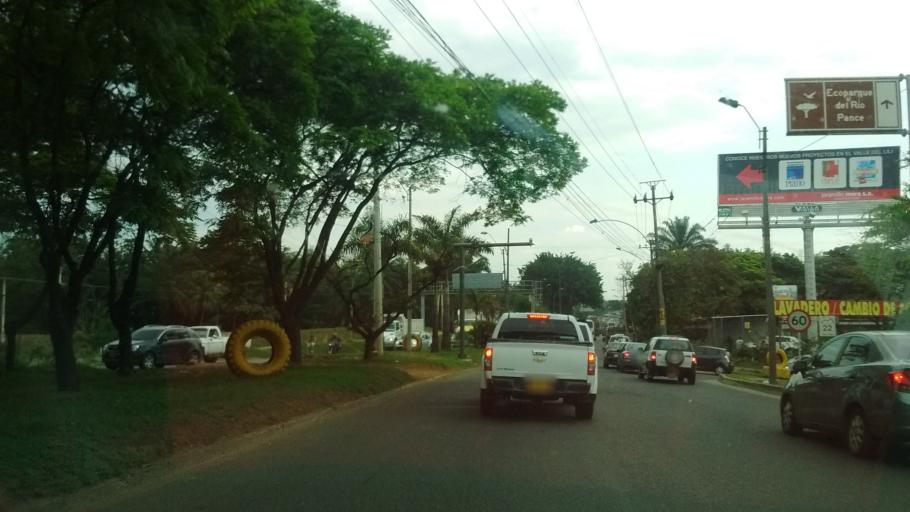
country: CO
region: Valle del Cauca
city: Cali
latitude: 3.3636
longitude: -76.5245
